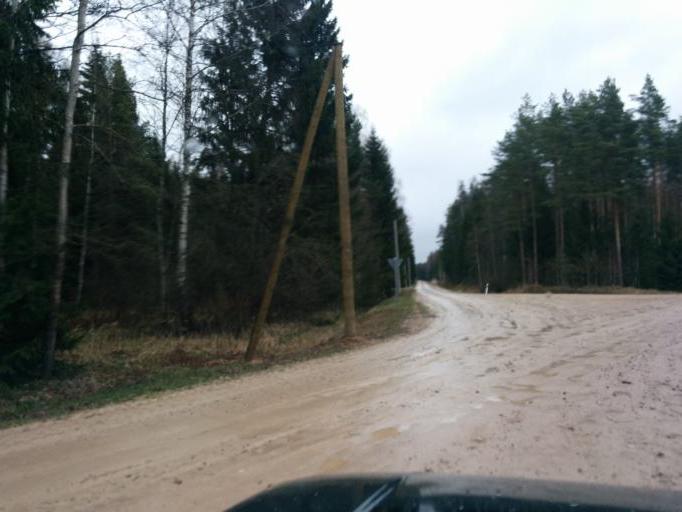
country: LV
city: Tireli
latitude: 56.8176
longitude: 23.6915
